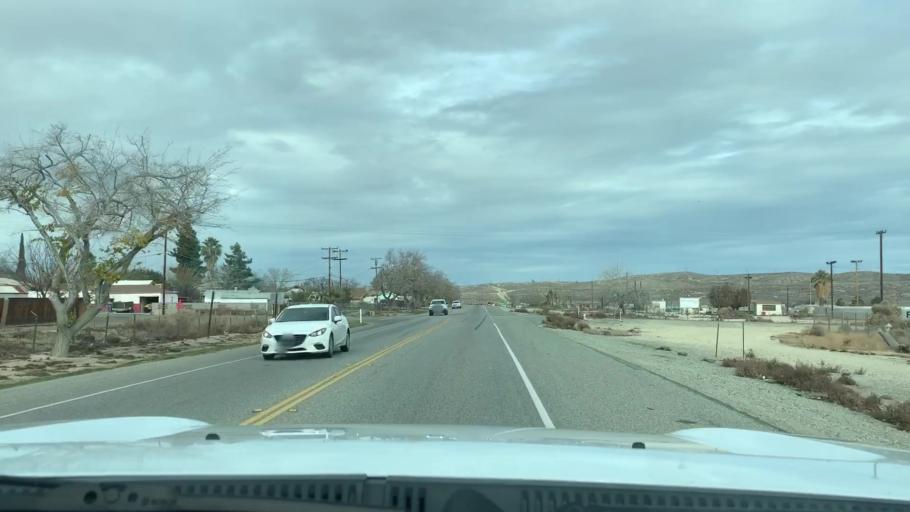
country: US
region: California
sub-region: Kern County
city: Ford City
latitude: 35.1508
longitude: -119.4479
